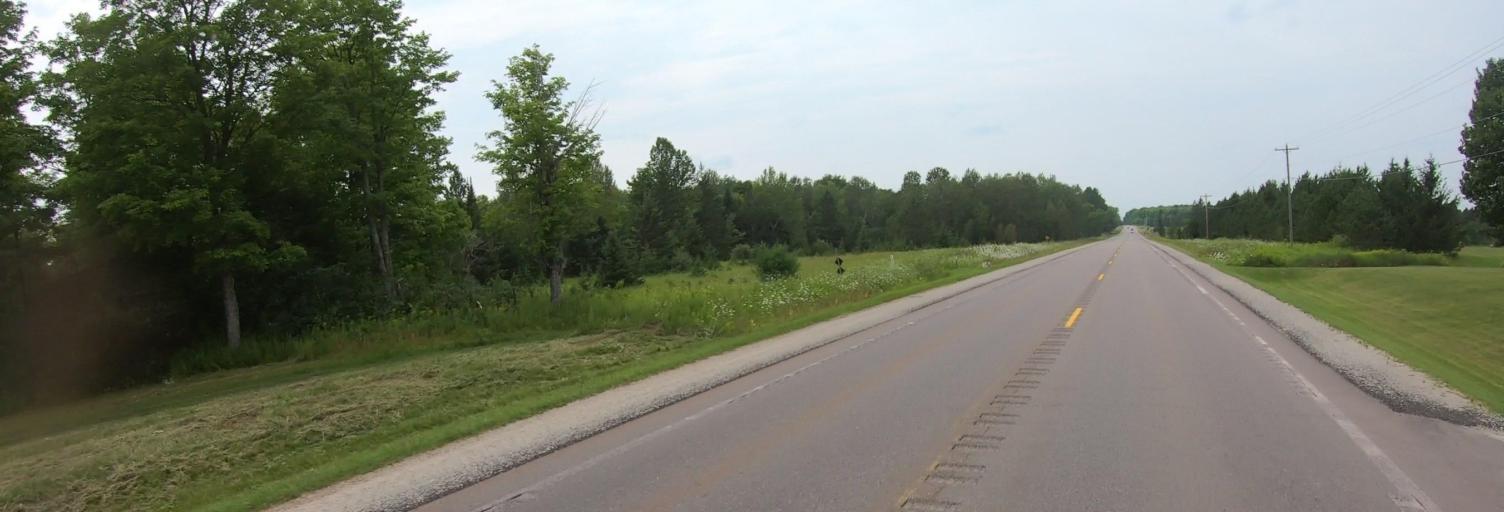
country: US
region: Michigan
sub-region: Alger County
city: Munising
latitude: 46.3548
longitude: -86.9820
